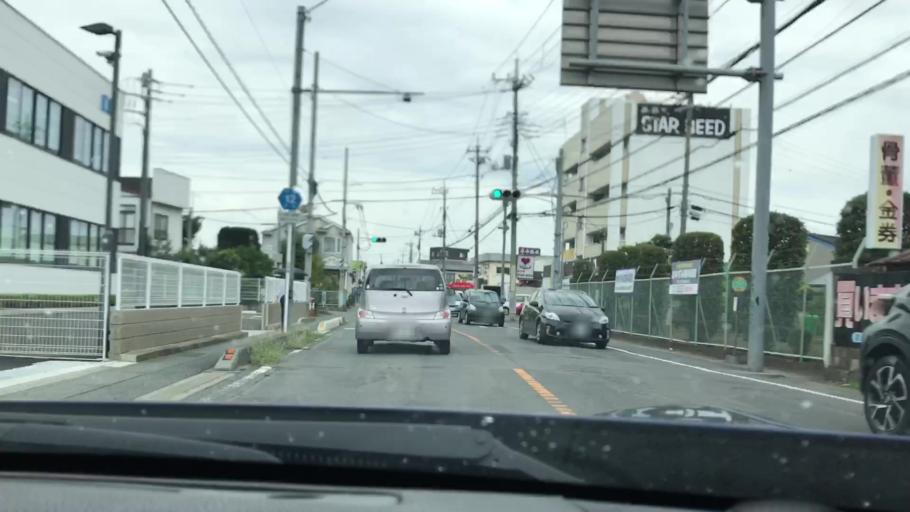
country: JP
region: Gunma
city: Takasaki
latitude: 36.3474
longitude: 139.0215
